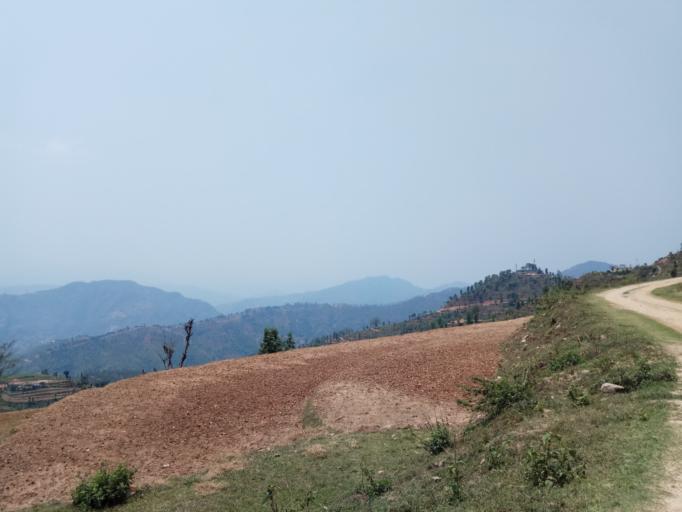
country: NP
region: Central Region
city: Kirtipur
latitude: 27.8964
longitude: 85.0745
